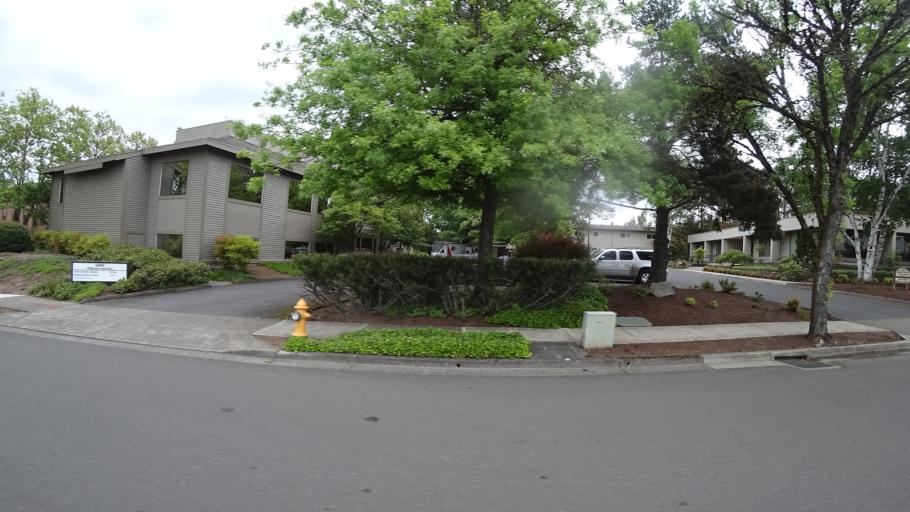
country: US
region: Oregon
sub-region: Washington County
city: Beaverton
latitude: 45.4708
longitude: -122.7853
